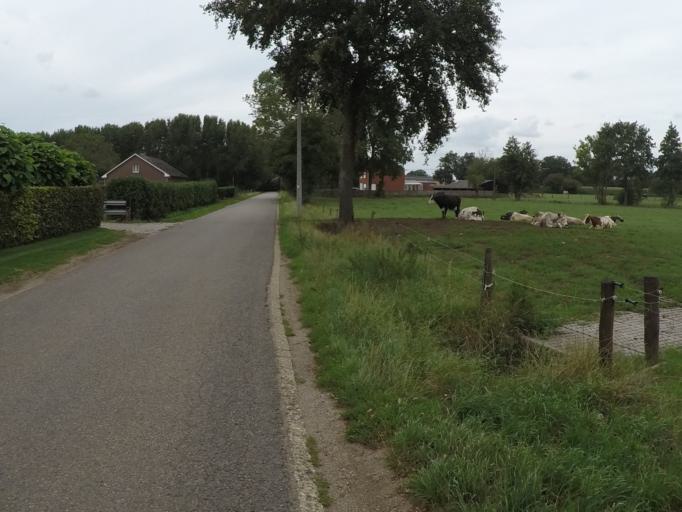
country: BE
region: Flanders
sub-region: Provincie Antwerpen
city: Vorselaar
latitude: 51.2266
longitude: 4.7775
